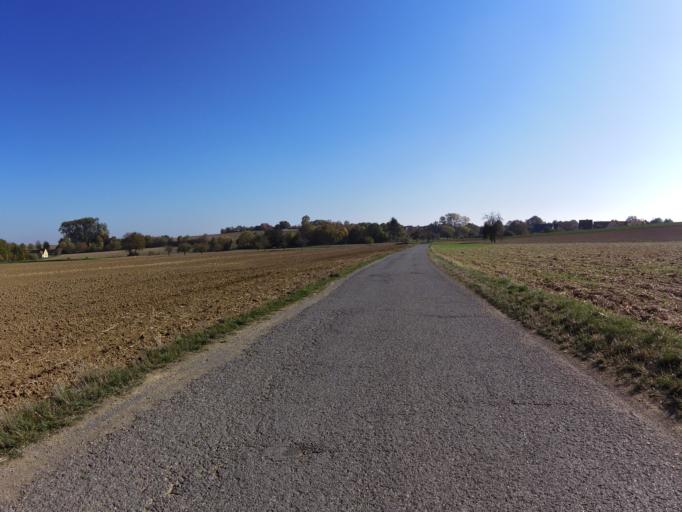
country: DE
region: Bavaria
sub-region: Regierungsbezirk Unterfranken
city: Geroldshausen
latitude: 49.6981
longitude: 9.9226
